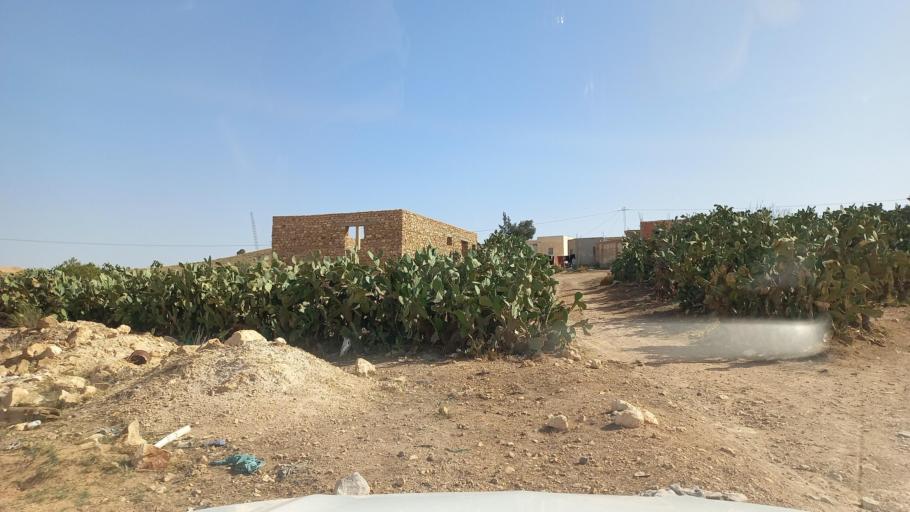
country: TN
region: Al Qasrayn
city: Kasserine
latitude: 35.2069
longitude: 8.9785
